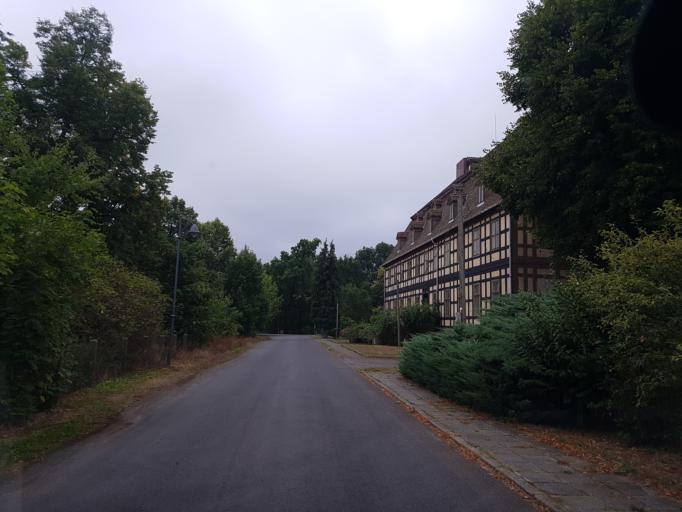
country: DE
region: Brandenburg
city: Calau
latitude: 51.7734
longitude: 13.8745
